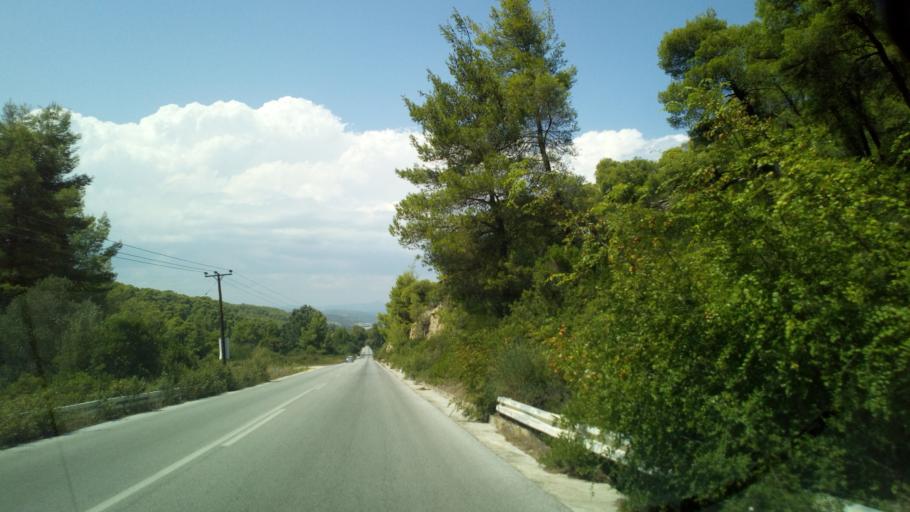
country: GR
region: Central Macedonia
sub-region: Nomos Chalkidikis
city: Agios Nikolaos
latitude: 40.2138
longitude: 23.7552
